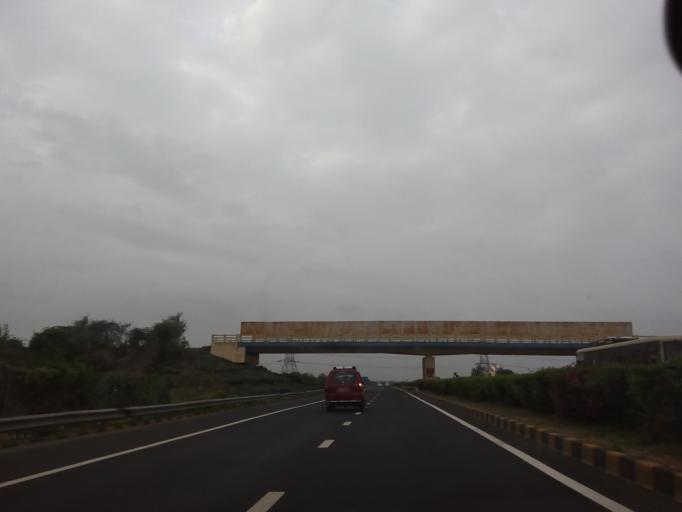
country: IN
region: Gujarat
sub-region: Kheda
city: Nadiad
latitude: 22.7622
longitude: 72.8546
